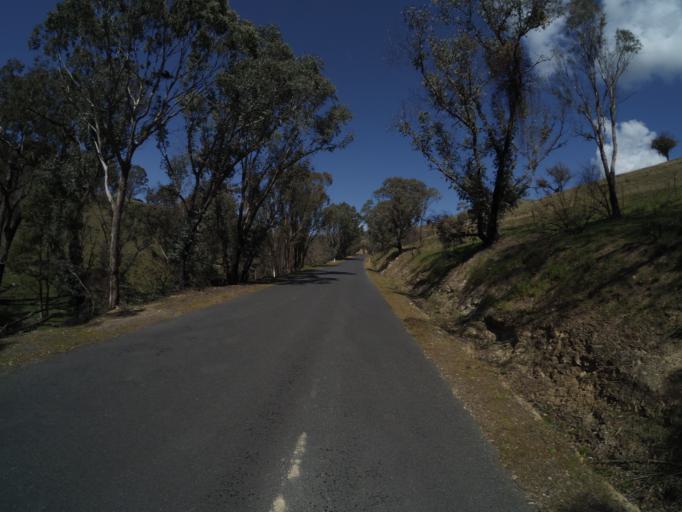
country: AU
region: New South Wales
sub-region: Yass Valley
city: Murrumbateman
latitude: -35.0897
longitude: 148.8461
